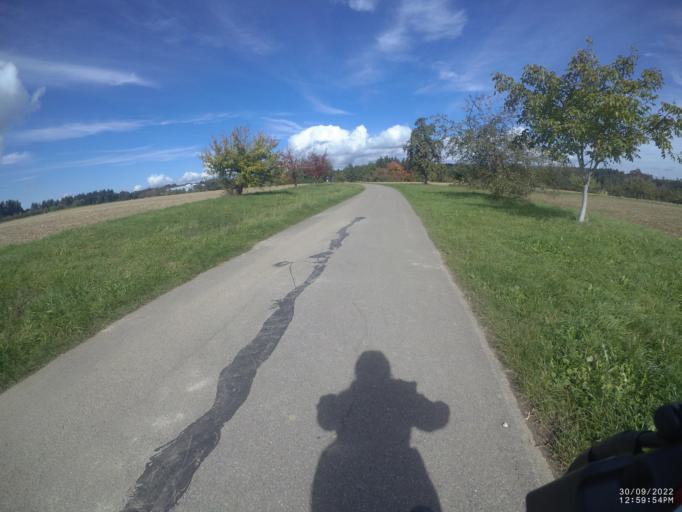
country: DE
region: Baden-Wuerttemberg
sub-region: Regierungsbezirk Stuttgart
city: Adelberg
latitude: 48.7690
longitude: 9.5961
